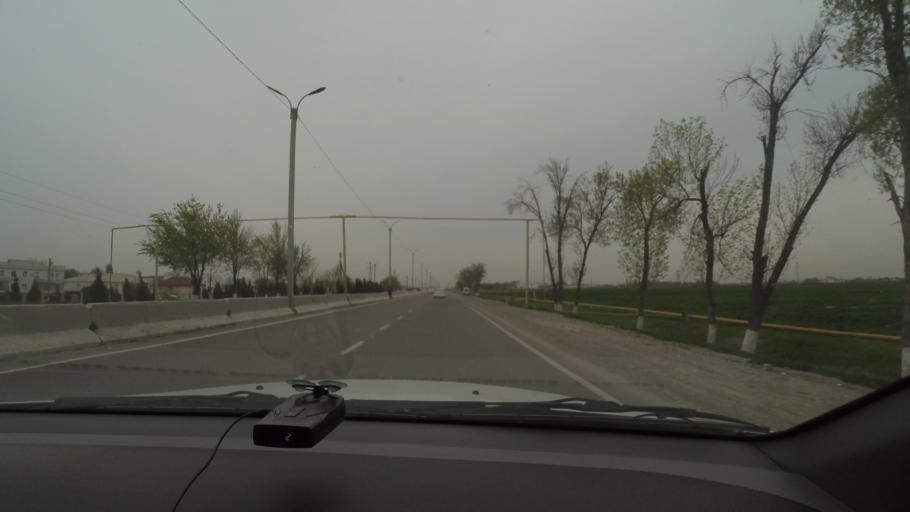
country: KZ
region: Ongtustik Qazaqstan
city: Myrzakent
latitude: 40.5517
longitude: 68.3996
